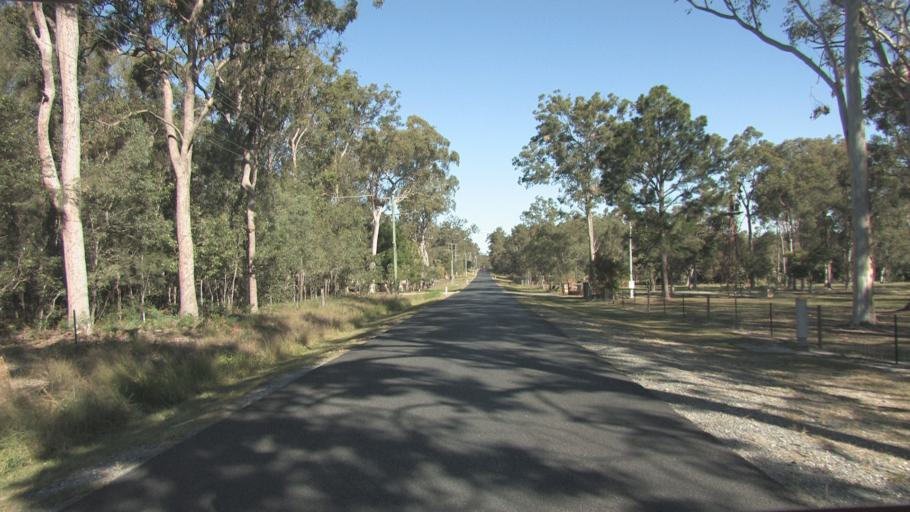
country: AU
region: Queensland
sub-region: Logan
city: Logan Reserve
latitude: -27.7271
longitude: 153.0729
